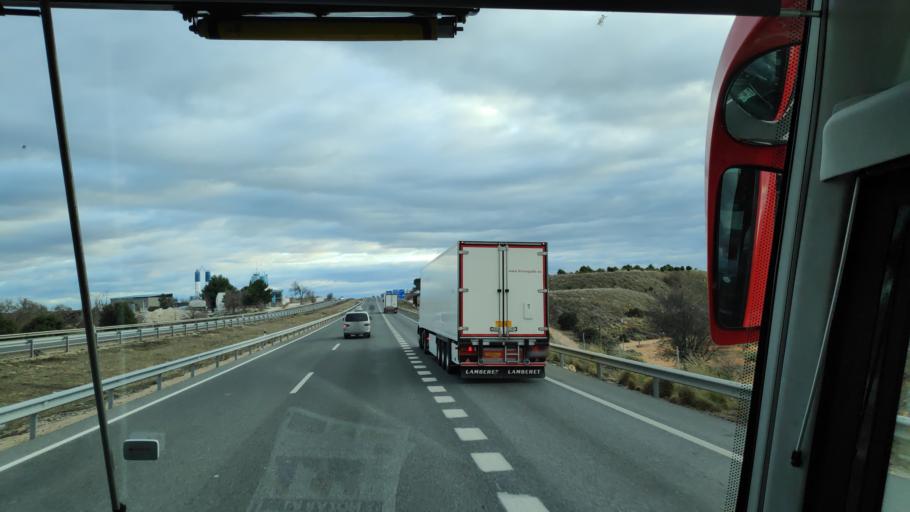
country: ES
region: Madrid
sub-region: Provincia de Madrid
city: Villarejo de Salvanes
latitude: 40.1868
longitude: -3.2984
